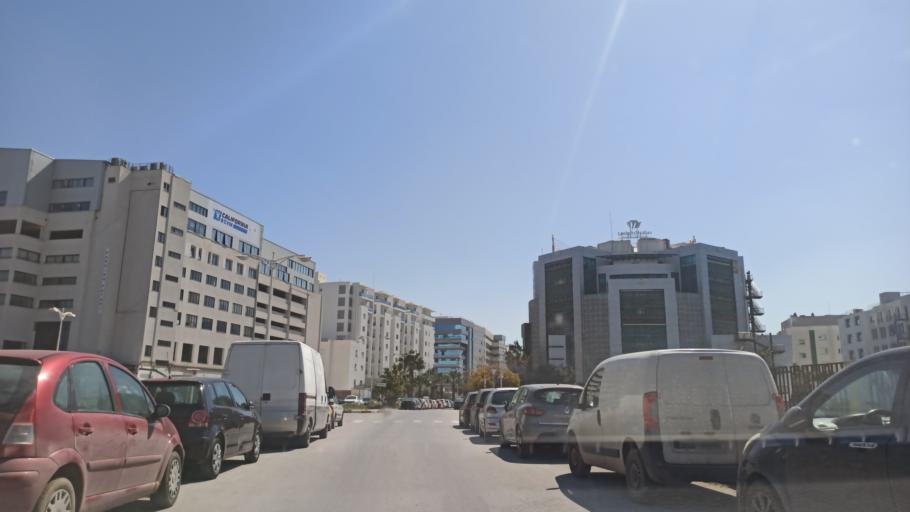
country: TN
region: Ariana
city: Ariana
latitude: 36.8505
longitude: 10.1969
